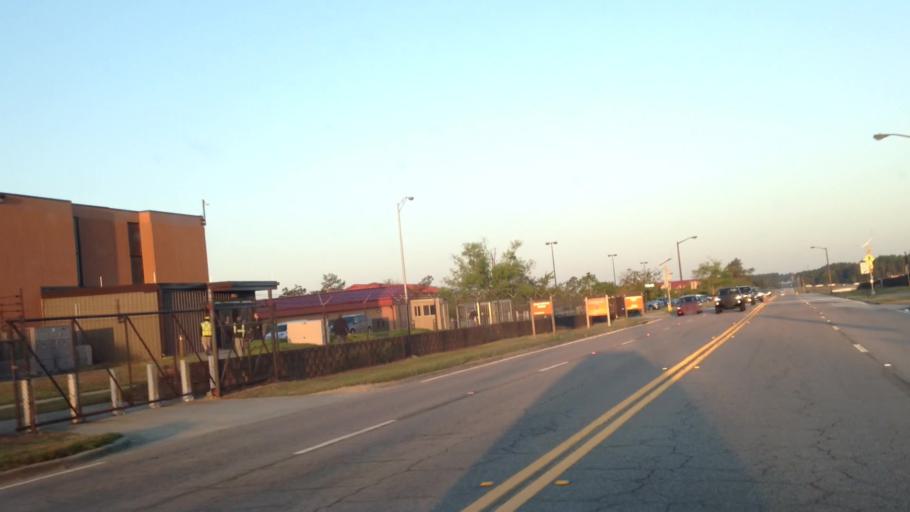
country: US
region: Georgia
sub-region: Columbia County
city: Grovetown
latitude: 33.4255
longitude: -82.1533
